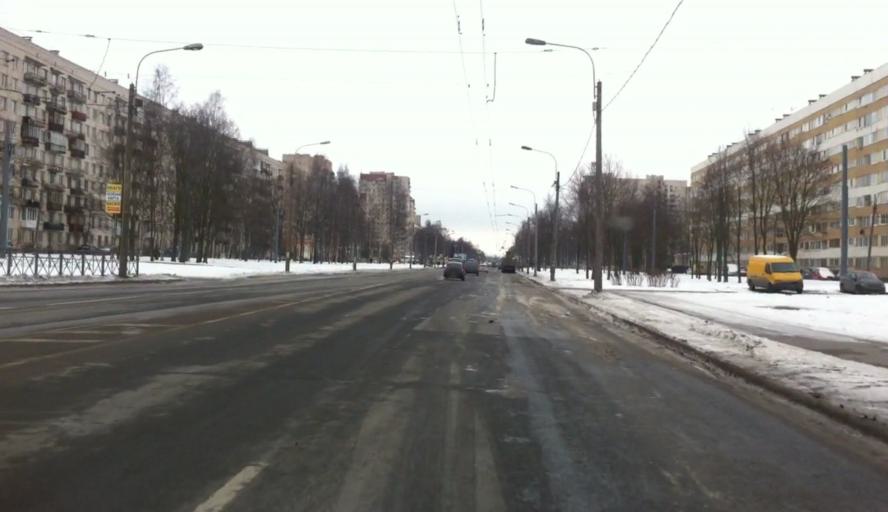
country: RU
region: St.-Petersburg
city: Uritsk
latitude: 59.8385
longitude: 30.1754
